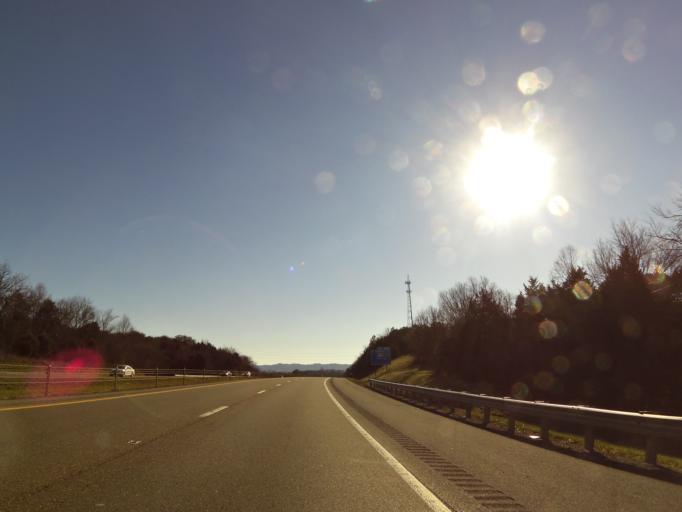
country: US
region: Tennessee
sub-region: Cocke County
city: Newport
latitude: 35.9674
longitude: -83.2255
